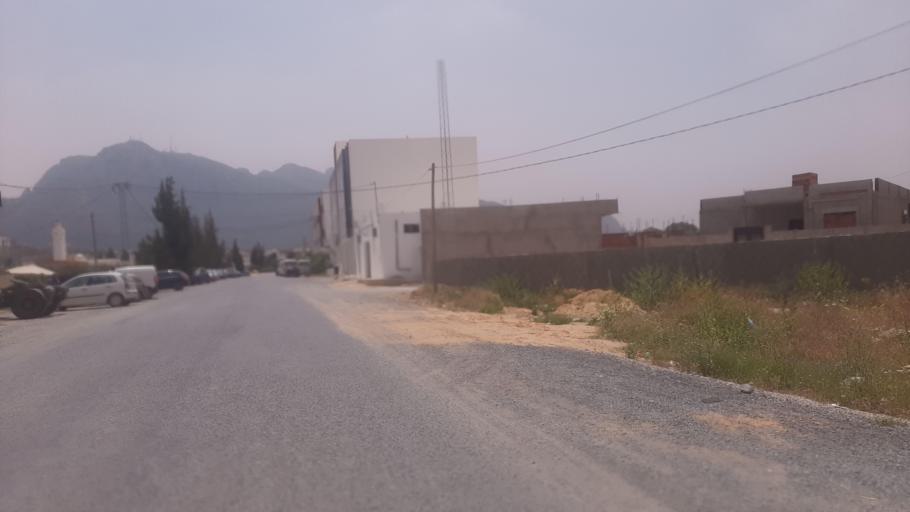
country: TN
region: Zaghwan
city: Zaghouan
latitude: 36.4152
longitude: 10.1357
